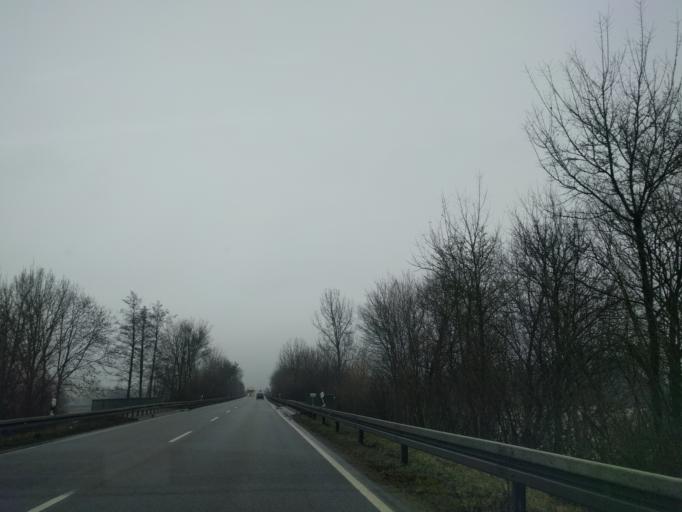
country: DE
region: Bavaria
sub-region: Lower Bavaria
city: Winzer
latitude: 48.7187
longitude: 13.0519
